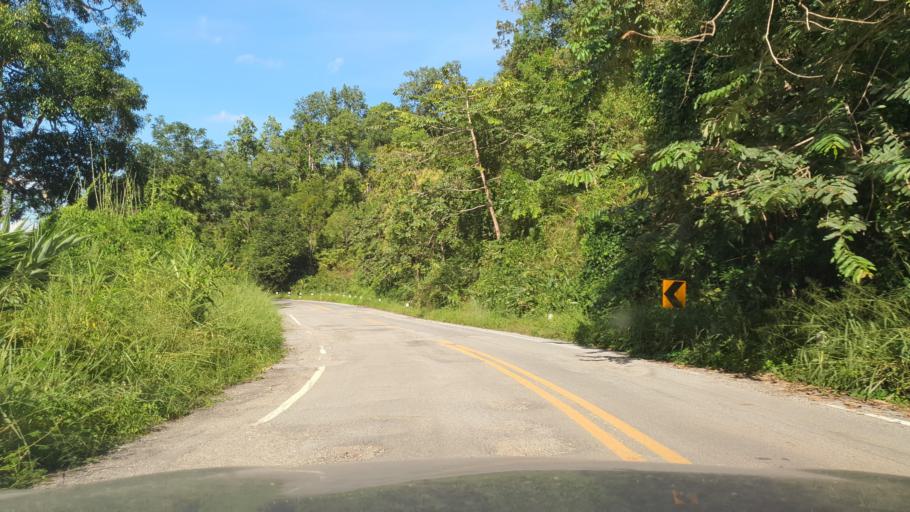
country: TH
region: Chiang Rai
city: Wiang Pa Pao
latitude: 19.3274
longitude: 99.4483
